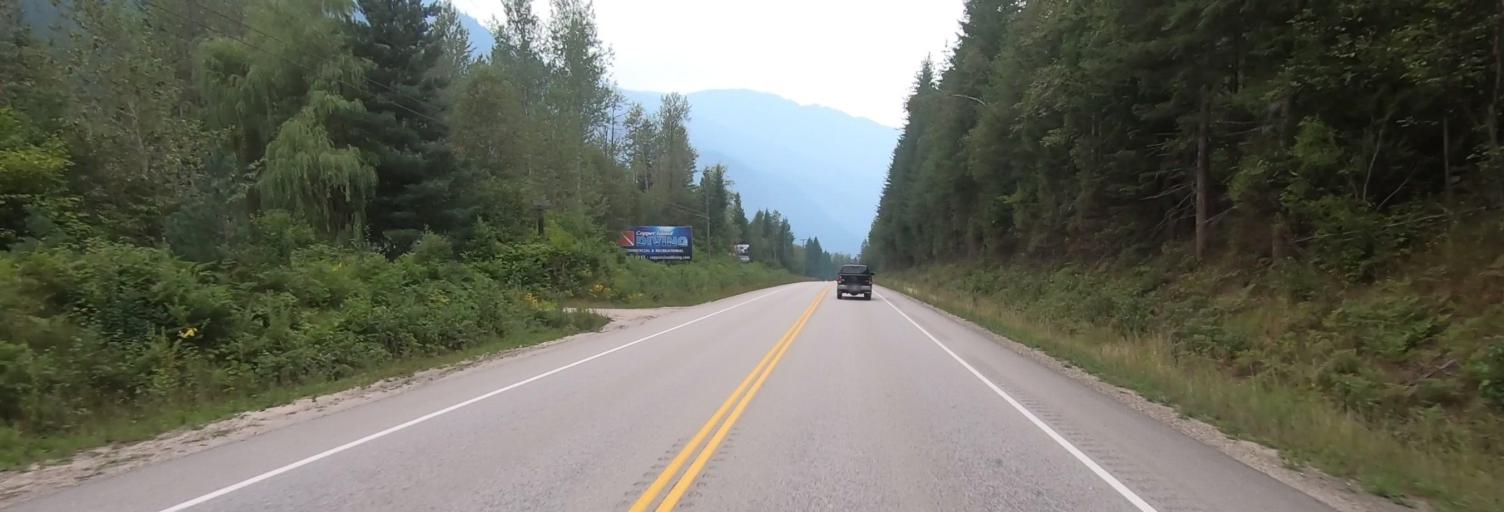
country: CA
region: British Columbia
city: Revelstoke
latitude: 50.9760
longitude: -118.5398
